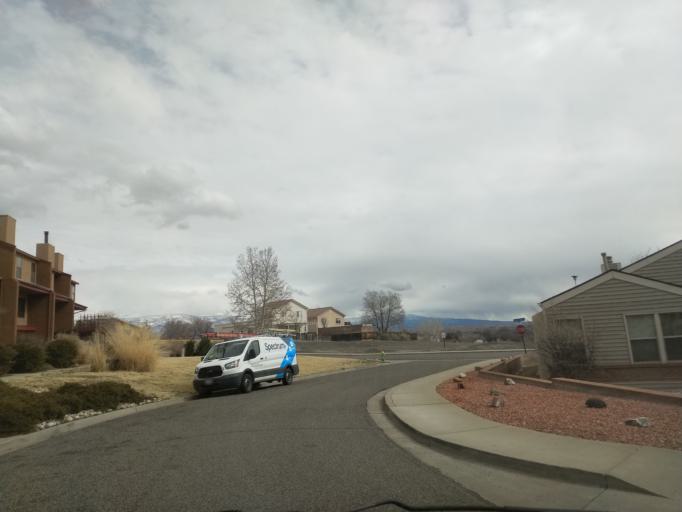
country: US
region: Colorado
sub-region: Mesa County
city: Fruitvale
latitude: 39.0902
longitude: -108.5273
